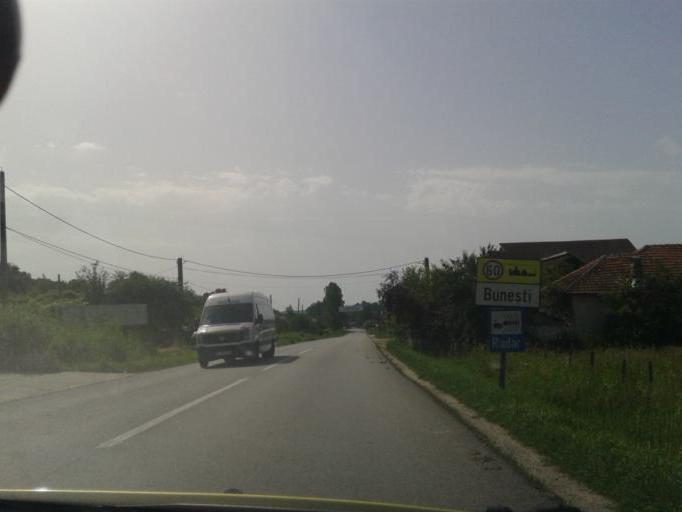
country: RO
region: Valcea
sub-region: Comuna Stoenesti
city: Stoenesti
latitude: 45.1150
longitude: 24.1722
